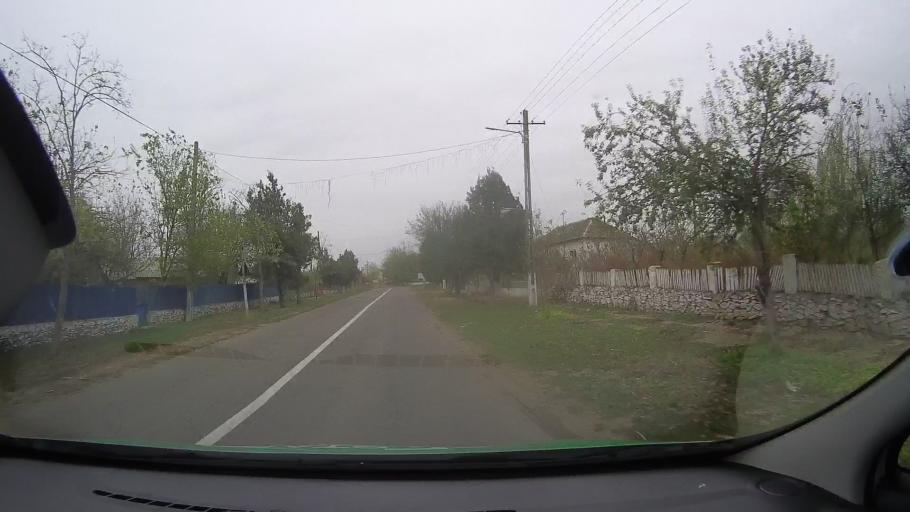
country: RO
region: Constanta
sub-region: Comuna Vulturu
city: Vulturu
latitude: 44.7054
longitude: 28.2342
